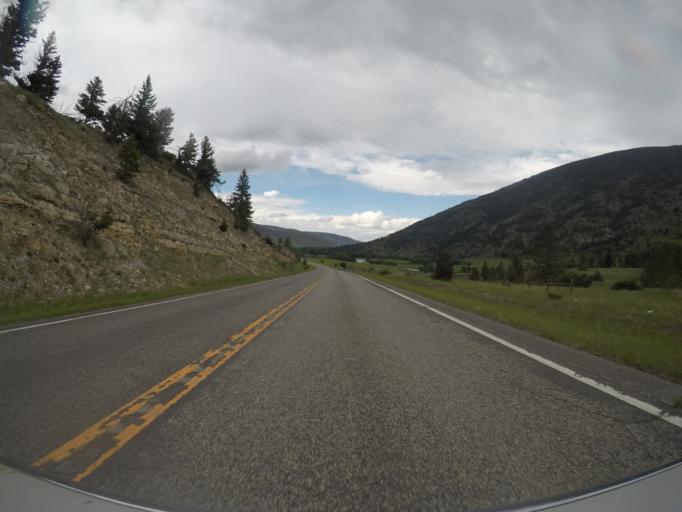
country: US
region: Montana
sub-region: Park County
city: Livingston
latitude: 45.5535
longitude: -110.2049
